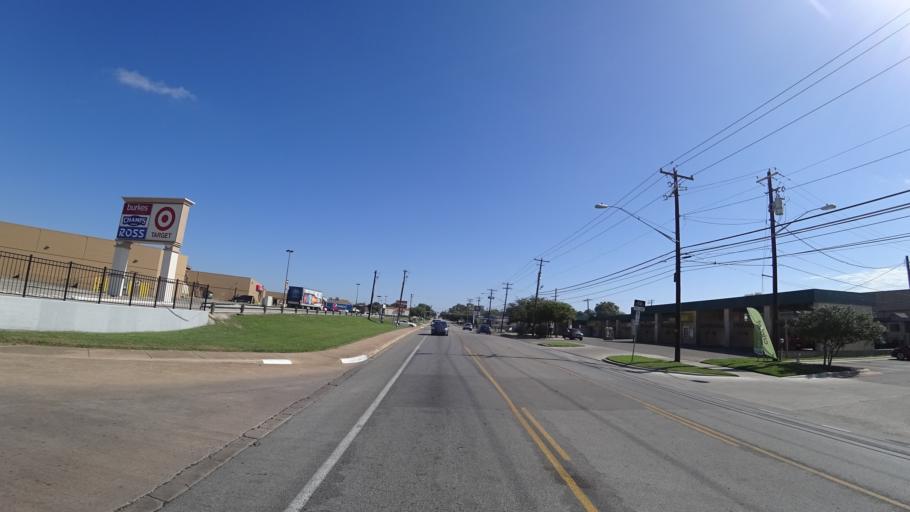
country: US
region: Texas
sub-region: Travis County
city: Austin
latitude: 30.3120
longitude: -97.7064
